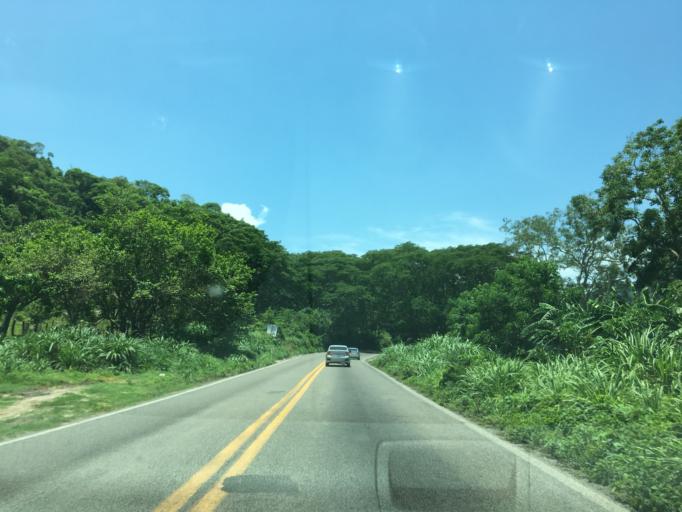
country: MX
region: Nayarit
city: Bucerias
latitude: 20.8288
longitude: -105.4047
